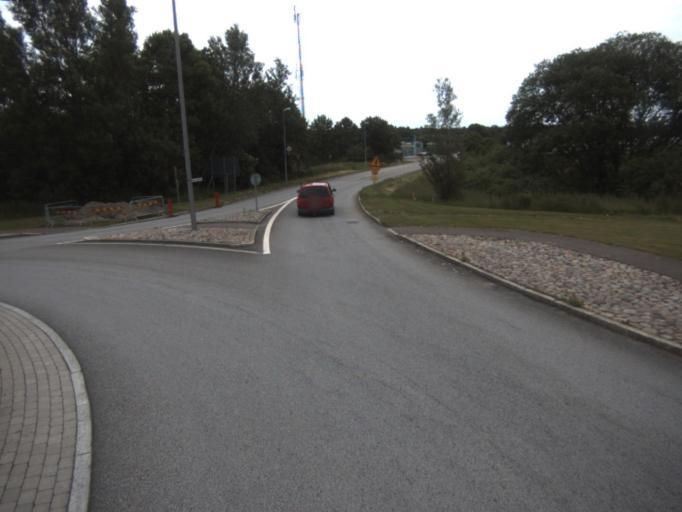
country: SE
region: Skane
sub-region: Helsingborg
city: Odakra
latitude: 56.0810
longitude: 12.7316
